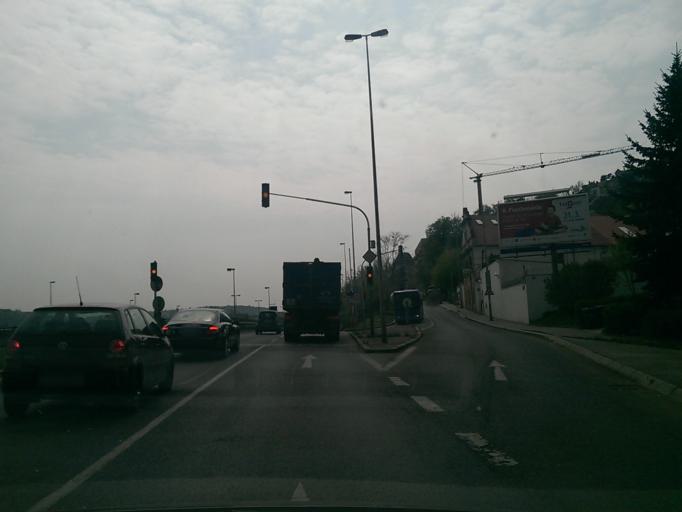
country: CZ
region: Praha
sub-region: Praha 2
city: Vysehrad
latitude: 50.0621
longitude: 14.4057
